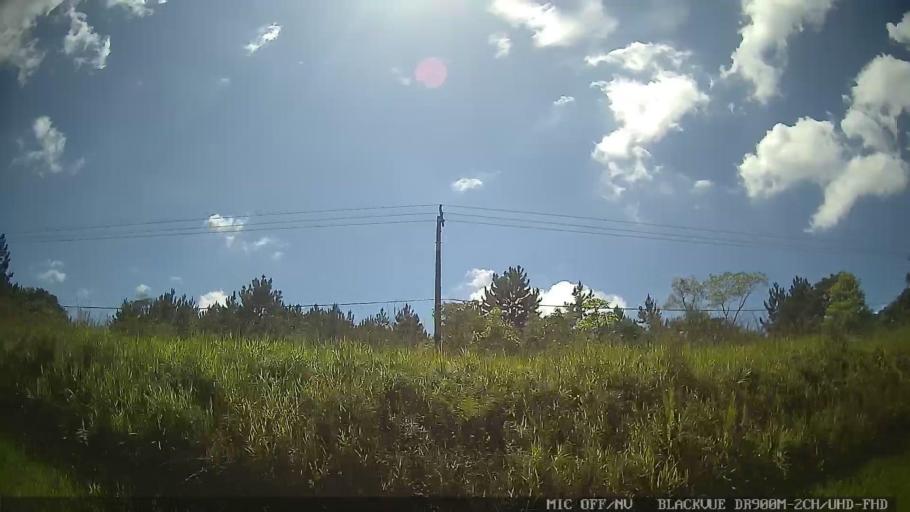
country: BR
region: Sao Paulo
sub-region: Mogi das Cruzes
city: Mogi das Cruzes
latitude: -23.6397
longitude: -46.2009
